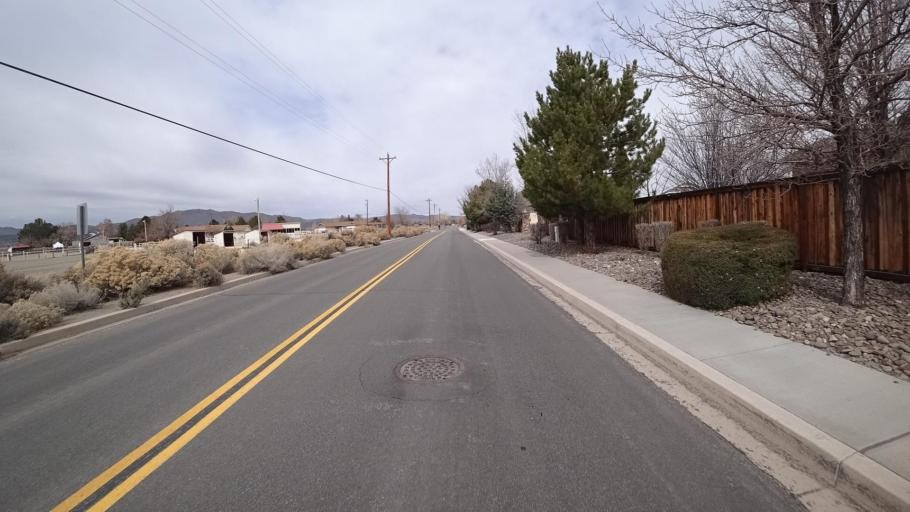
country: US
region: Nevada
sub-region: Washoe County
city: Spanish Springs
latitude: 39.6263
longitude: -119.6873
